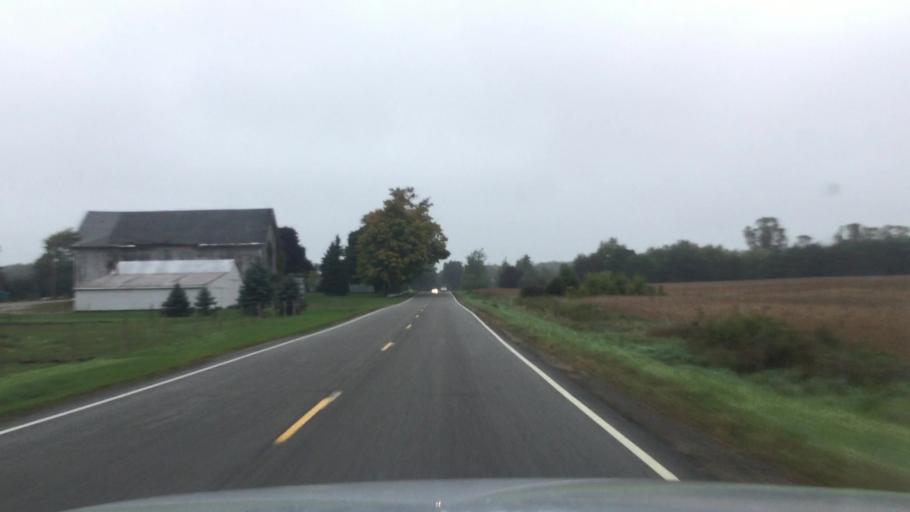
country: US
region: Michigan
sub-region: Shiawassee County
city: Corunna
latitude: 42.9246
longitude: -84.1242
